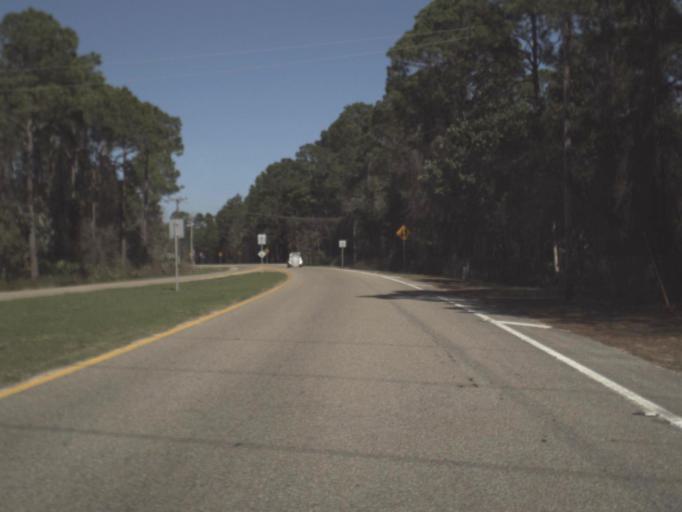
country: US
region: Florida
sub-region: Gulf County
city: Port Saint Joe
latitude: 29.8165
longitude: -85.2874
